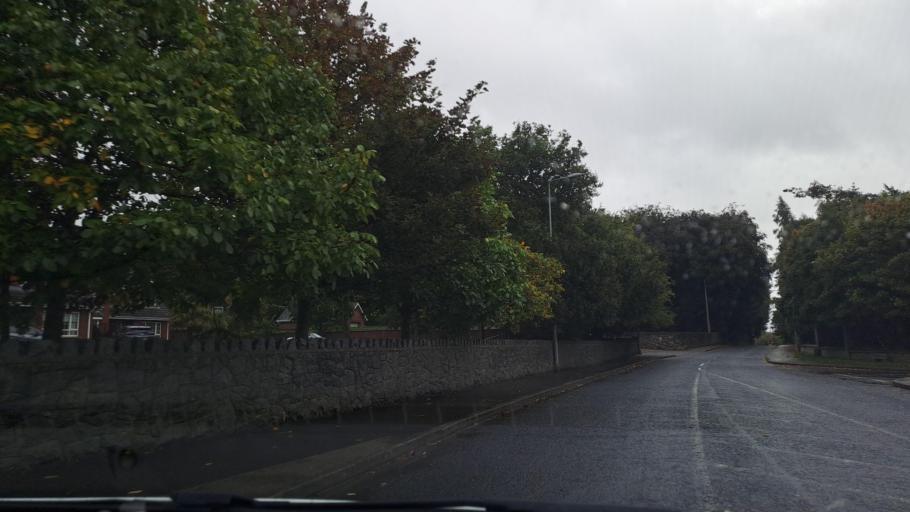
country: IE
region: Leinster
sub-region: Lu
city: Blackrock
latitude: 53.9607
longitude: -6.3760
